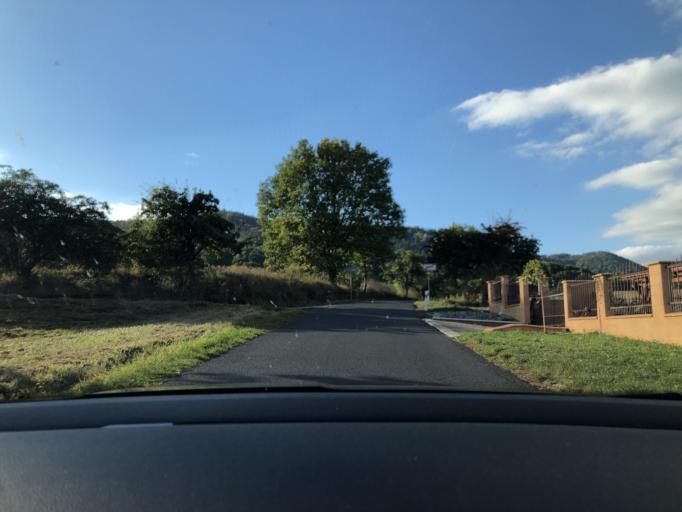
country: CZ
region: Ustecky
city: Zitenice
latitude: 50.5726
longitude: 14.1803
